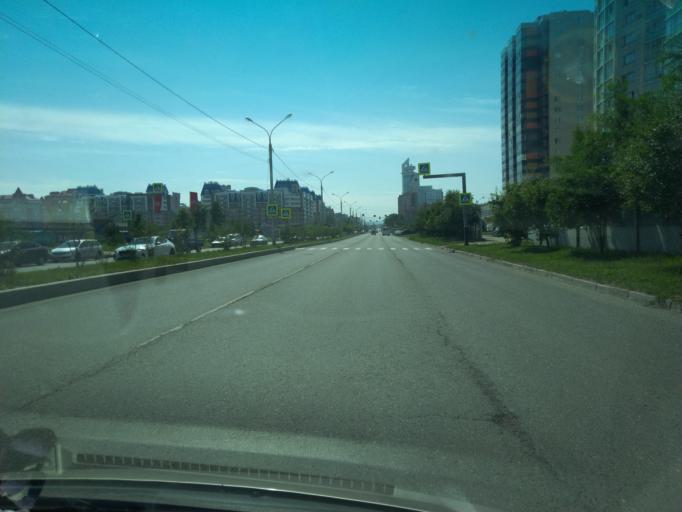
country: RU
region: Krasnoyarskiy
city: Krasnoyarsk
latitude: 56.0488
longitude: 92.9194
